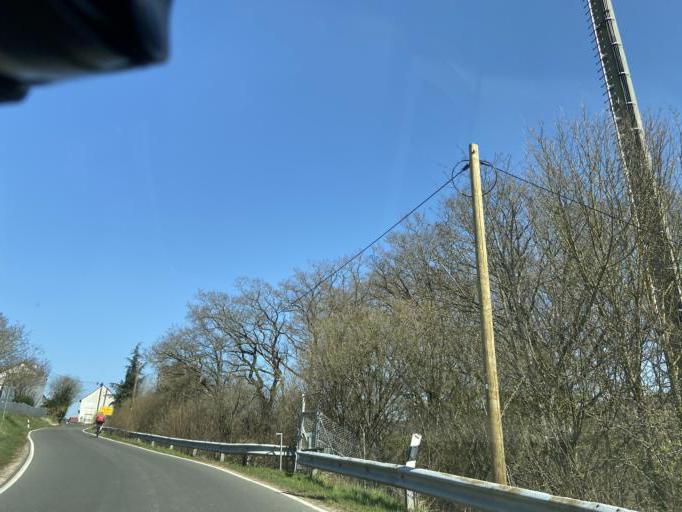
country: DE
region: Rheinland-Pfalz
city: Newel
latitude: 49.7950
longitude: 6.5848
